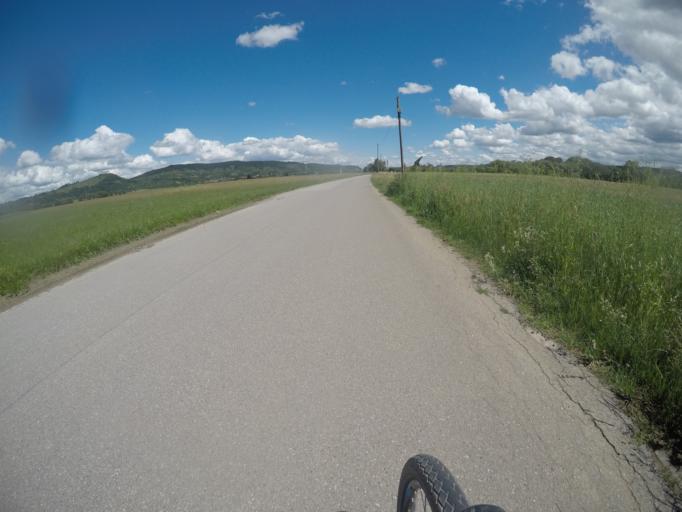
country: DE
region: Baden-Wuerttemberg
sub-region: Tuebingen Region
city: Rottenburg
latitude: 48.4879
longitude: 8.9733
